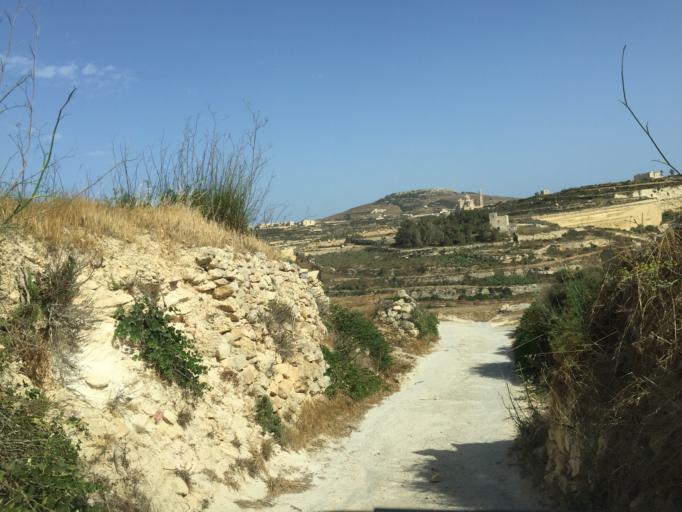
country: MT
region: L-Gharb
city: Gharb
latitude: 36.0702
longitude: 14.2062
